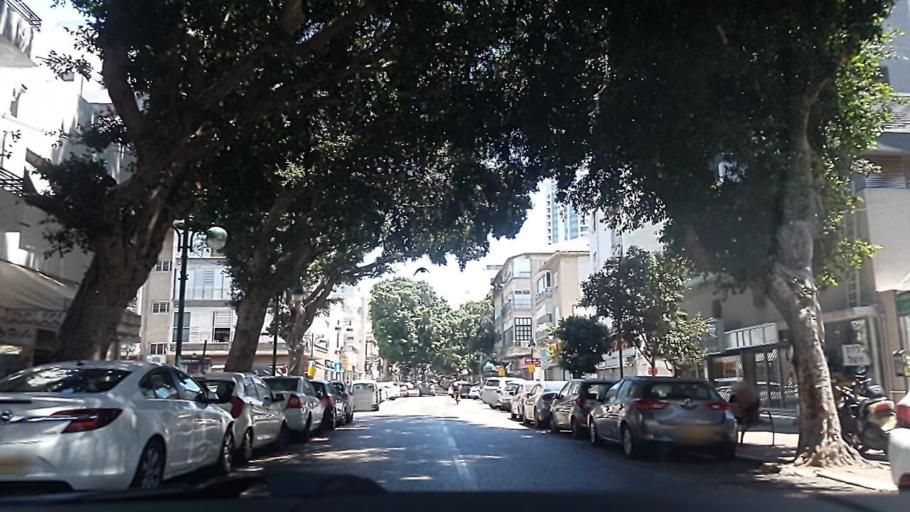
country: IL
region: Tel Aviv
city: Ramat Gan
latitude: 32.0853
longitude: 34.8117
